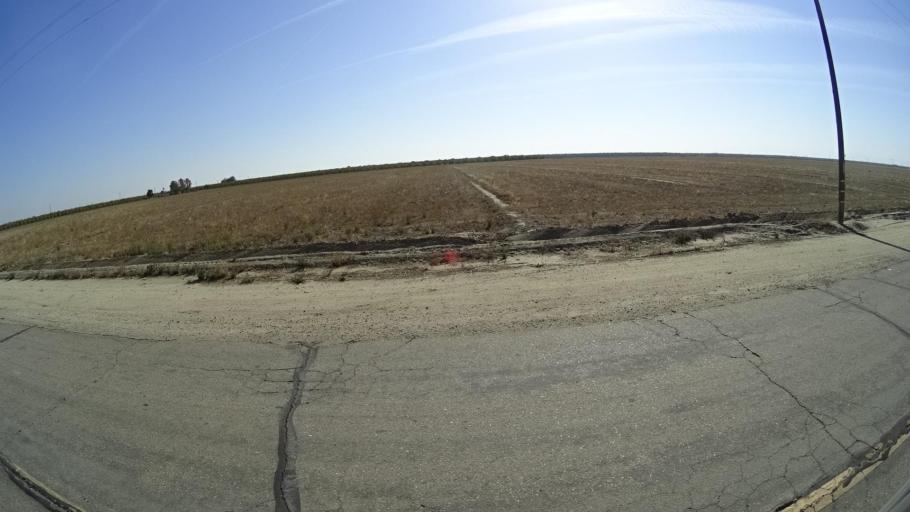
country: US
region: California
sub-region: Kern County
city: Wasco
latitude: 35.6670
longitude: -119.3783
